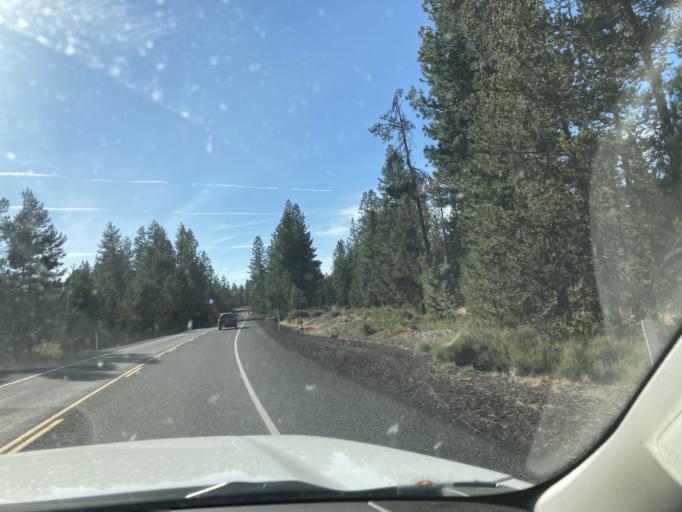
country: US
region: Oregon
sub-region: Deschutes County
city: Three Rivers
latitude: 43.8160
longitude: -121.4932
